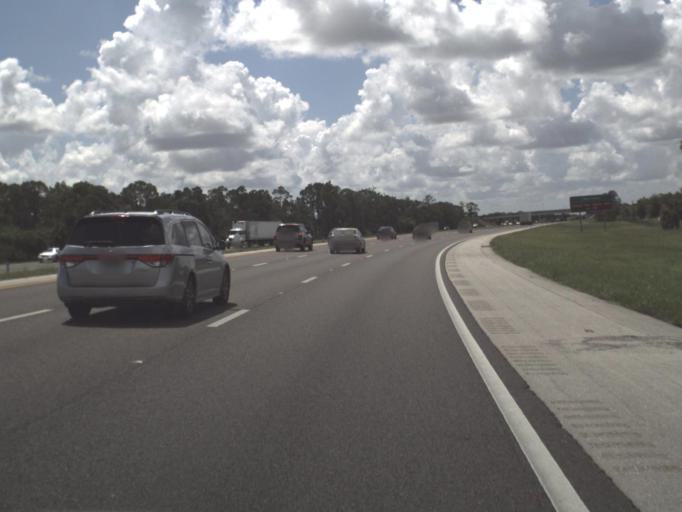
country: US
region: Florida
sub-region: Lee County
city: Bonita Springs
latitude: 26.3517
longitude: -81.7550
